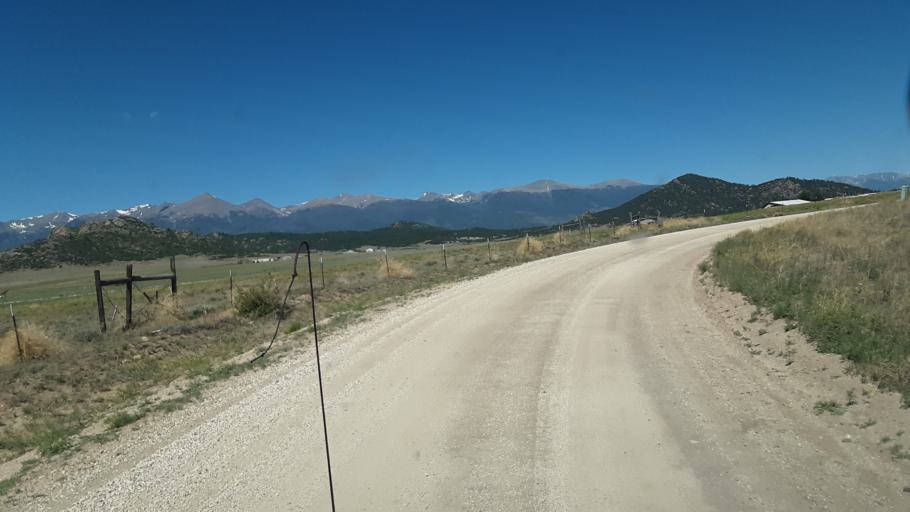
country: US
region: Colorado
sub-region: Custer County
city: Westcliffe
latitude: 38.2352
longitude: -105.4870
